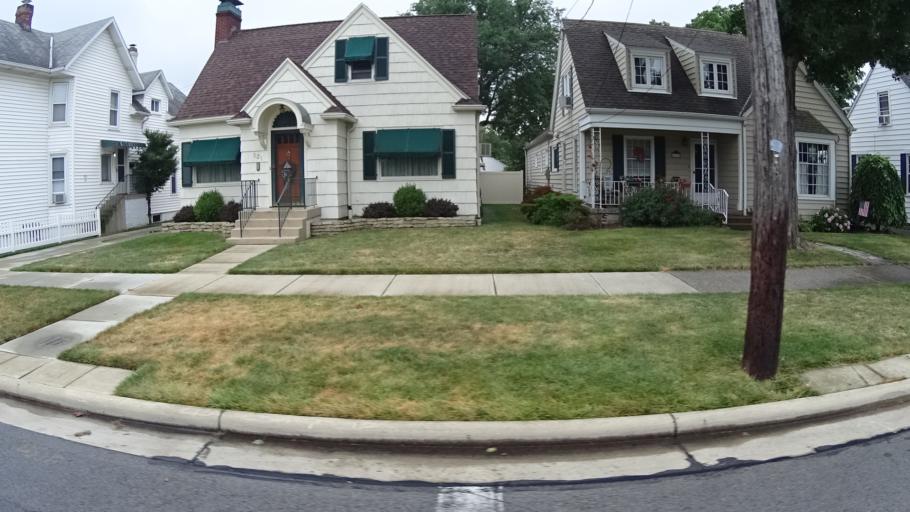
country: US
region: Ohio
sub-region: Erie County
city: Sandusky
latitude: 41.4498
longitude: -82.7155
